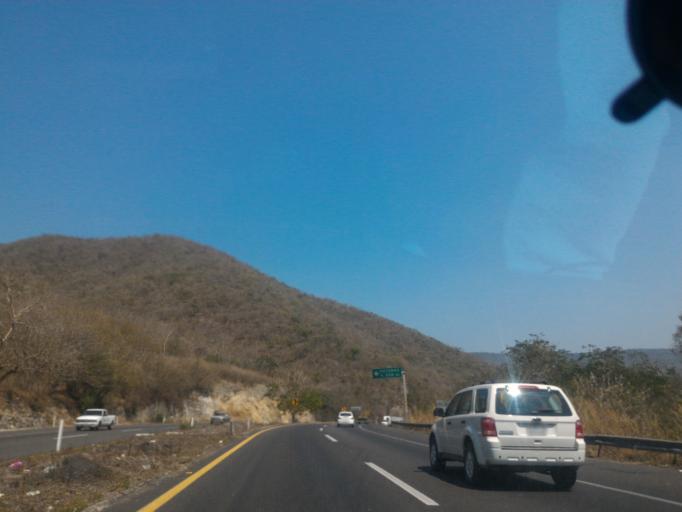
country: MX
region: Colima
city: Ixtlahuacan
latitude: 19.0239
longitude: -103.8050
